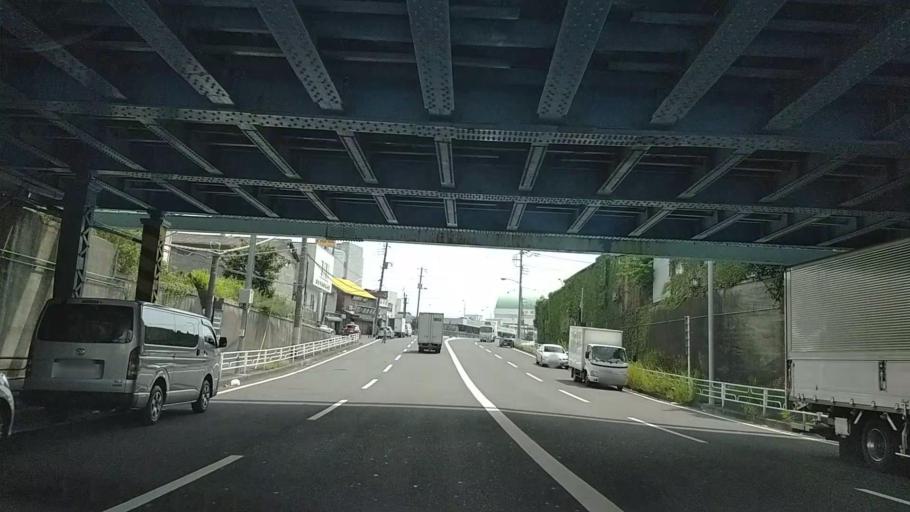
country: JP
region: Kanagawa
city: Yokohama
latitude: 35.4695
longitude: 139.6342
